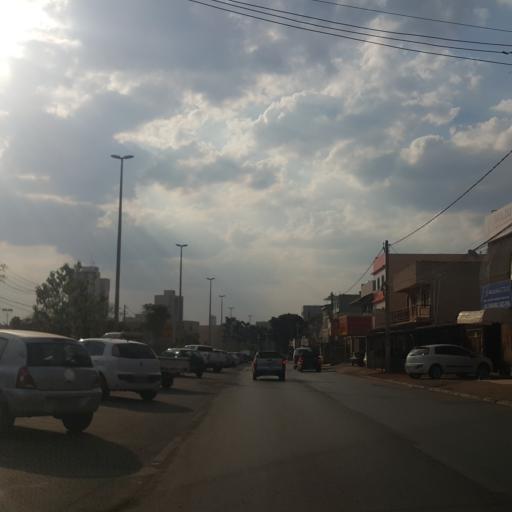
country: BR
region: Federal District
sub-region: Brasilia
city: Brasilia
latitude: -15.8604
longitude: -48.0273
